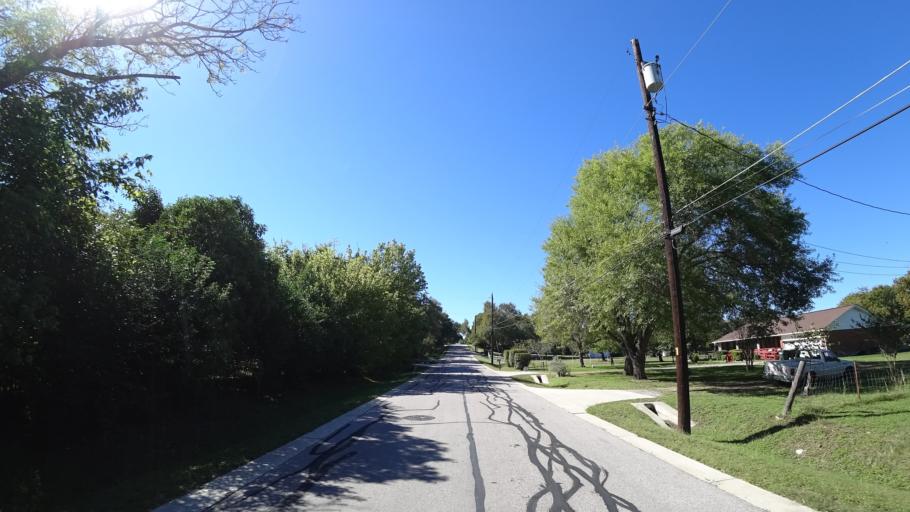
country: US
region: Texas
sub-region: Travis County
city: Rollingwood
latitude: 30.2246
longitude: -97.8098
